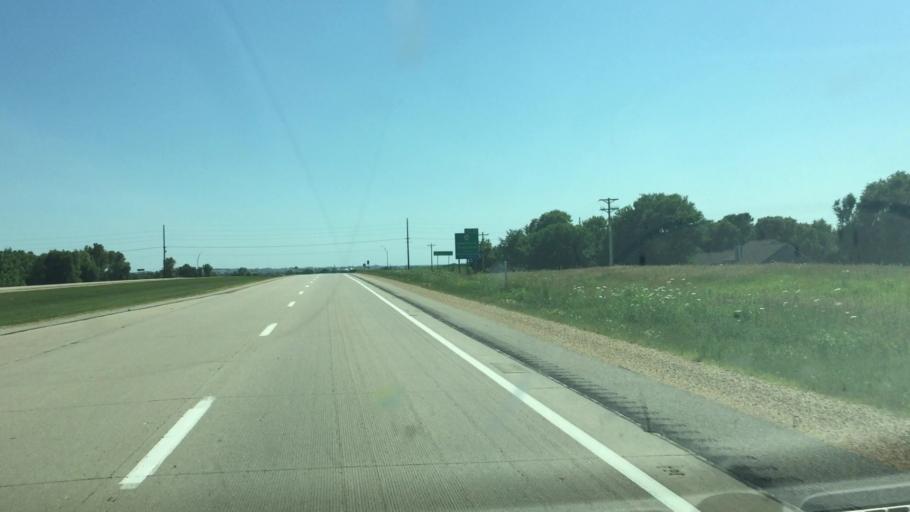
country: US
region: Iowa
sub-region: Jones County
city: Monticello
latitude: 42.2532
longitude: -91.1592
